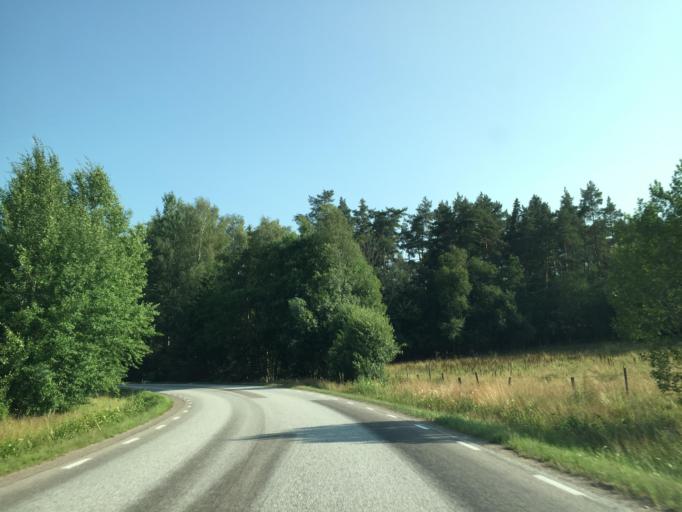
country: SE
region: Vaestra Goetaland
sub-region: Trollhattan
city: Trollhattan
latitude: 58.3085
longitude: 12.2528
